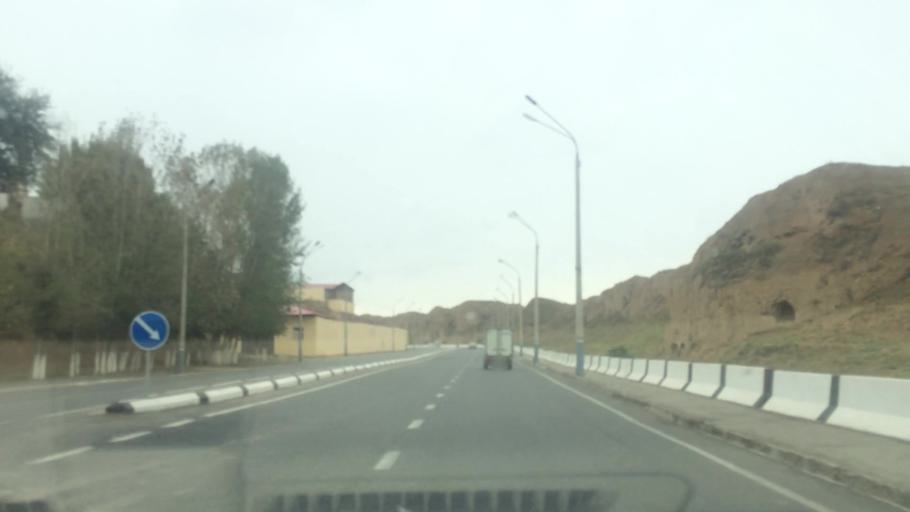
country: UZ
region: Samarqand
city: Samarqand
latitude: 39.6689
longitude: 66.9978
